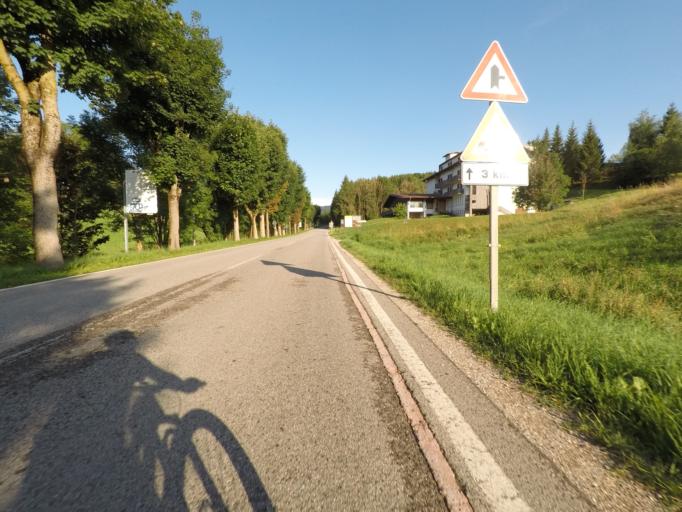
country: IT
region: Veneto
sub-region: Provincia di Vicenza
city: Asiago
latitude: 45.8679
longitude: 11.5178
